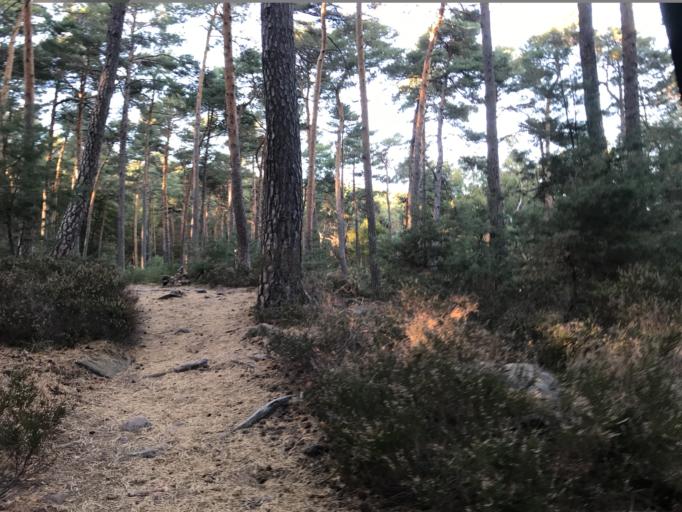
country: DE
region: Rheinland-Pfalz
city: Neustadt
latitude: 49.3634
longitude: 8.1225
